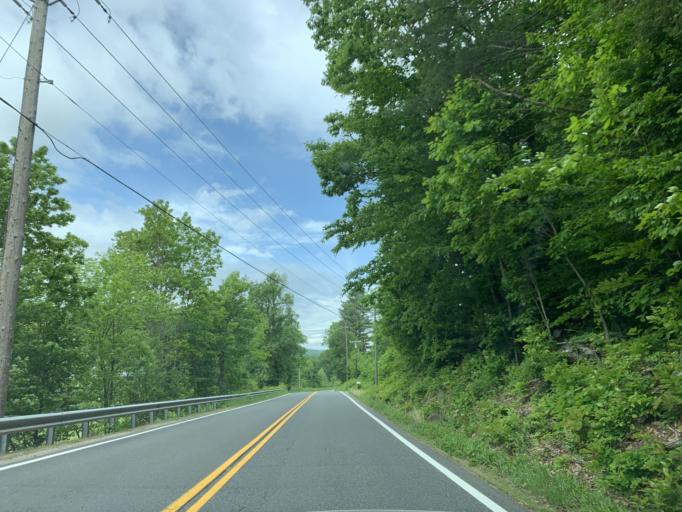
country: US
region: Massachusetts
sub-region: Hampshire County
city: Westhampton
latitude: 42.2454
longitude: -72.8640
